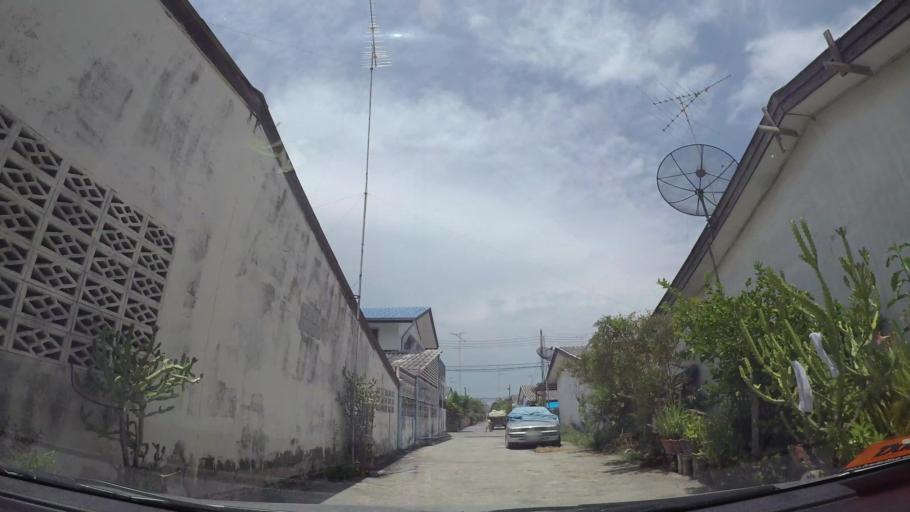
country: TH
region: Chon Buri
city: Chon Buri
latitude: 13.3303
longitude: 100.9422
